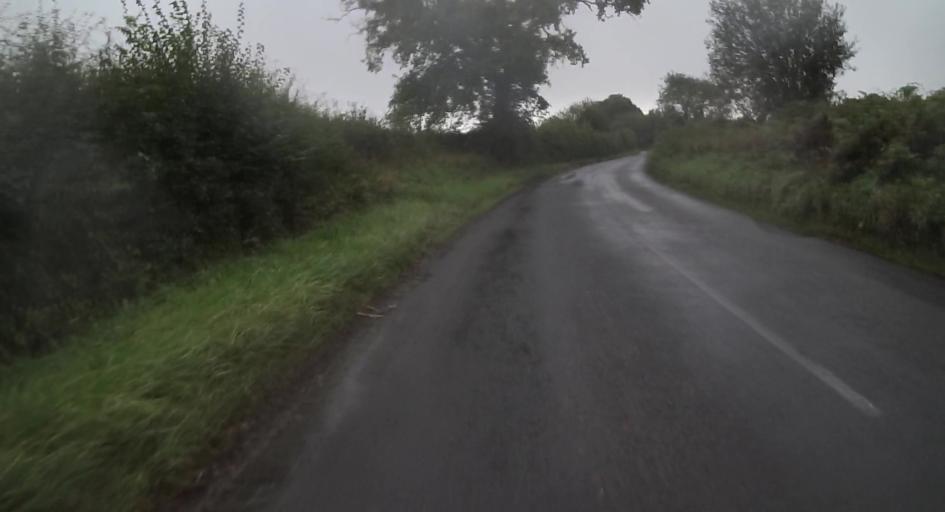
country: GB
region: England
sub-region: Hampshire
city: Tadley
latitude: 51.3095
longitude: -1.1384
